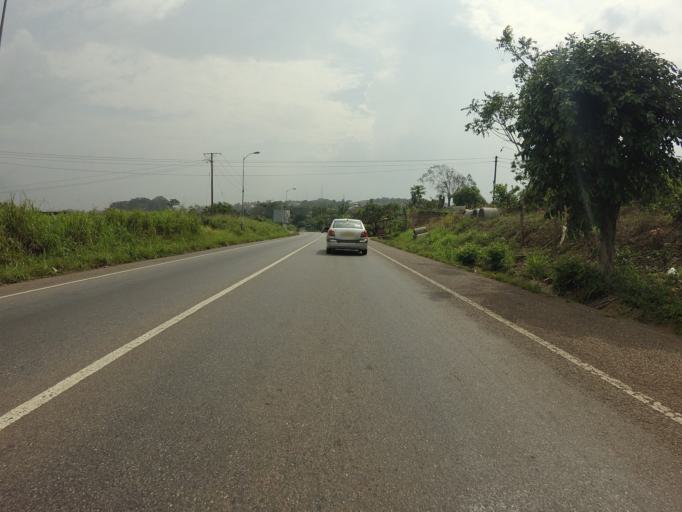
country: GH
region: Eastern
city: Aburi
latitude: 5.8241
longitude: -0.1862
